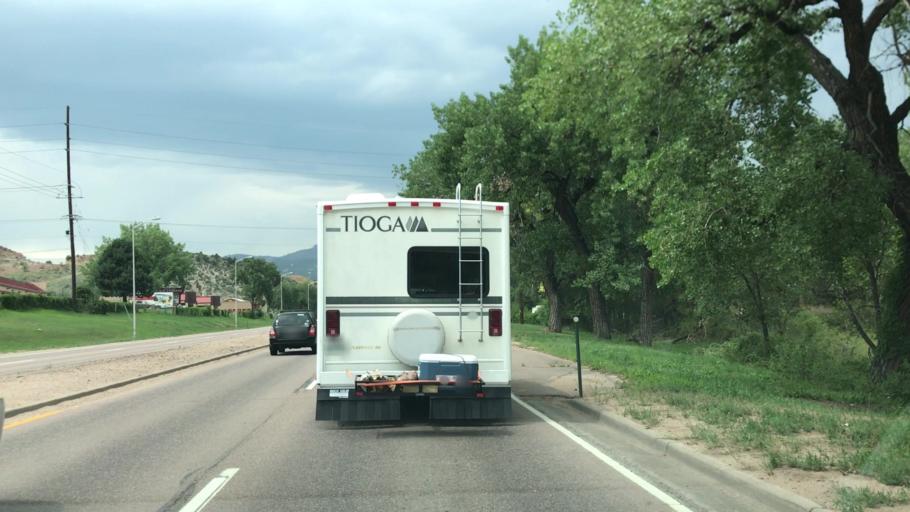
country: US
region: Colorado
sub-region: El Paso County
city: Colorado Springs
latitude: 38.8473
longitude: -104.8683
